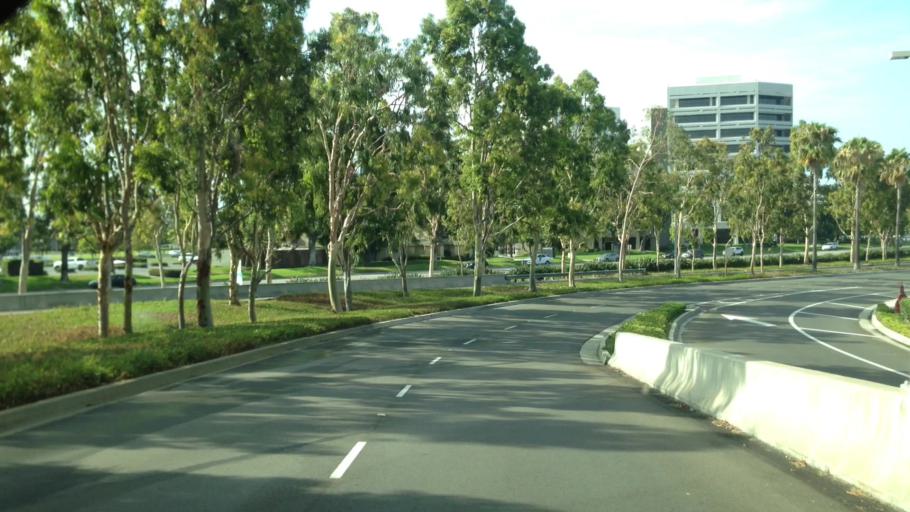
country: US
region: California
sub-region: Orange County
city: Irvine
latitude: 33.6749
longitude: -117.8633
